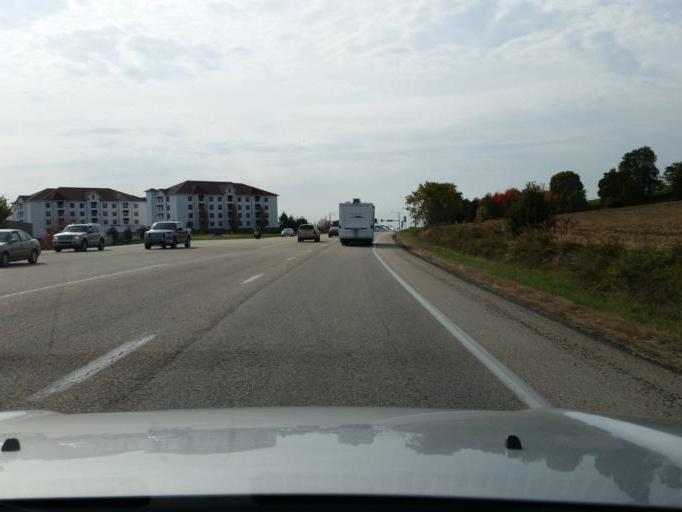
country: US
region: Pennsylvania
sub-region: Dauphin County
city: Hershey
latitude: 40.2987
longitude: -76.6424
